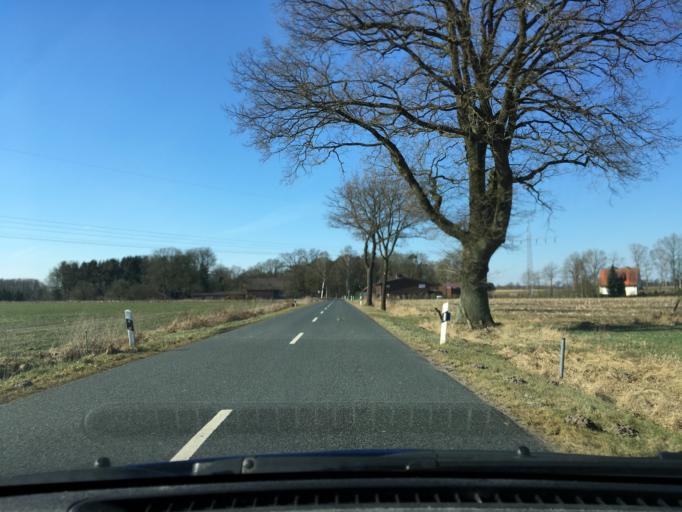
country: DE
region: Lower Saxony
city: Neuenkirchen
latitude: 53.0709
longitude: 9.6847
